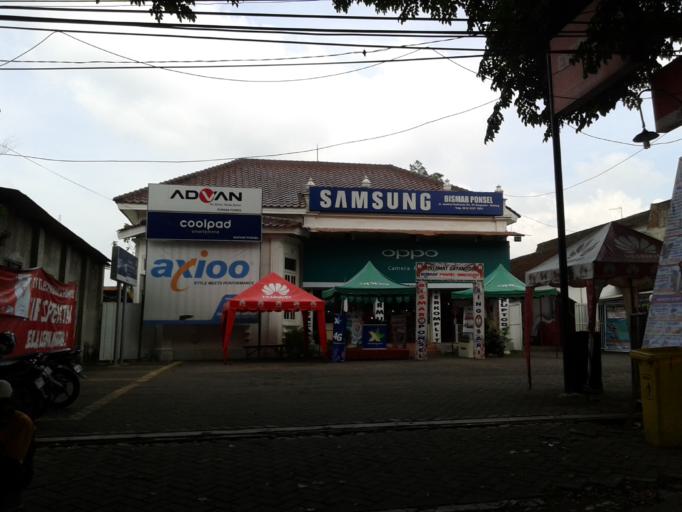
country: ID
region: East Java
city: Singosari
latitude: -7.8992
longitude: 112.6636
